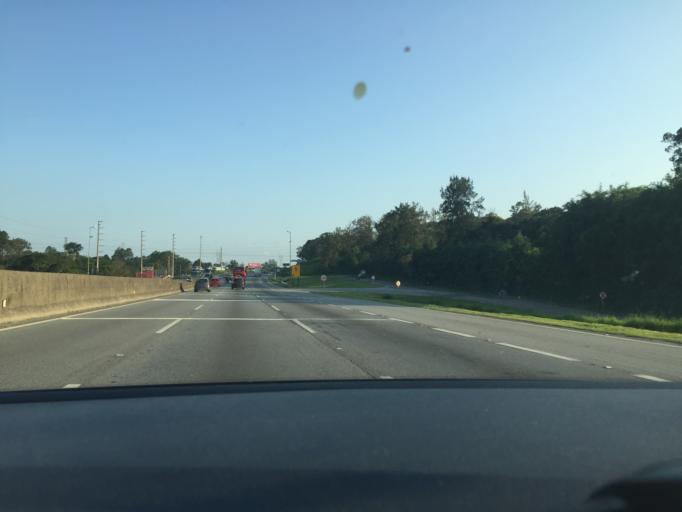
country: BR
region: Sao Paulo
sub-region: Louveira
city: Louveira
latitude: -23.1111
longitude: -46.9592
